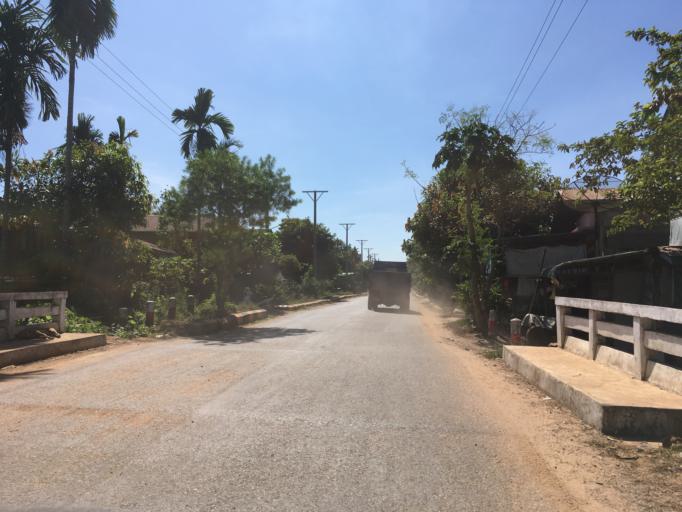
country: MM
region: Mon
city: Kyaikkami
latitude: 15.5064
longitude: 97.8389
